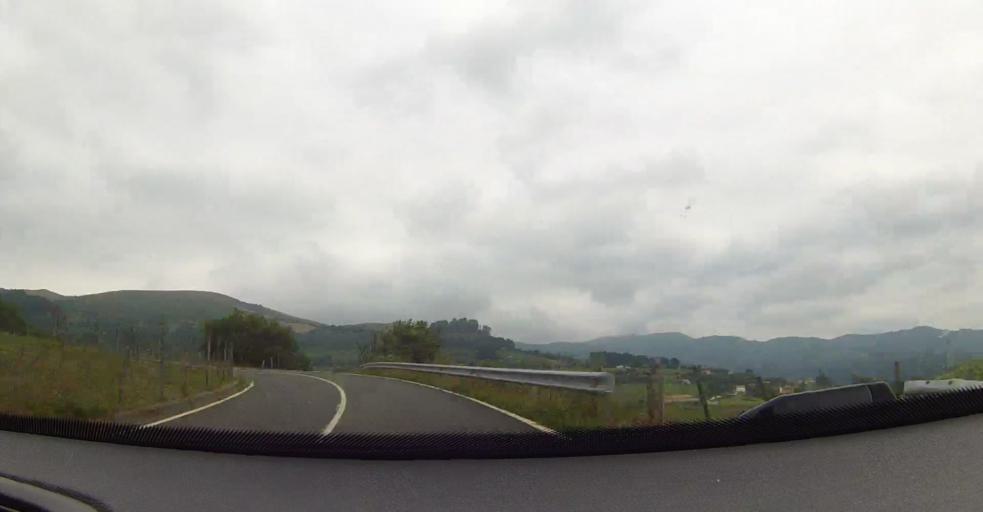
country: ES
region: Cantabria
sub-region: Provincia de Cantabria
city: Rasines
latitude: 43.2577
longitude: -3.3687
